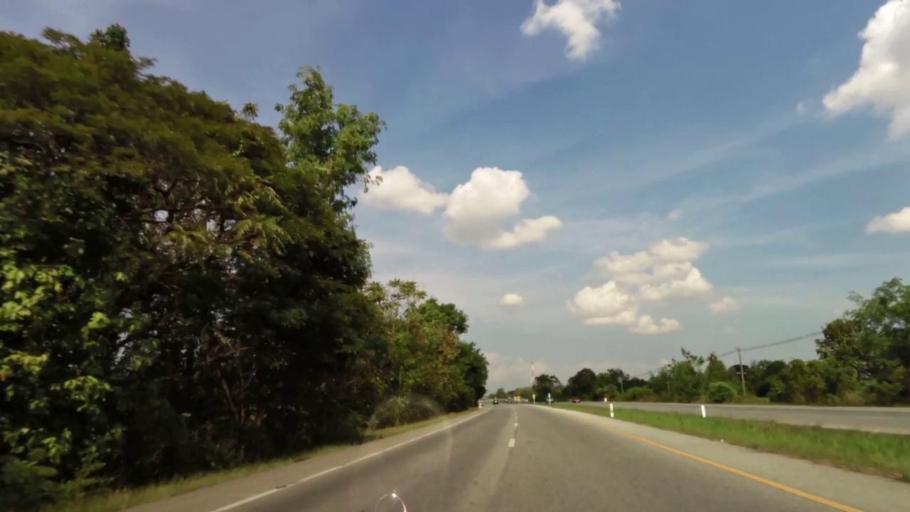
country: TH
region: Uttaradit
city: Thong Saen Khan
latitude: 17.4596
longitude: 100.2377
